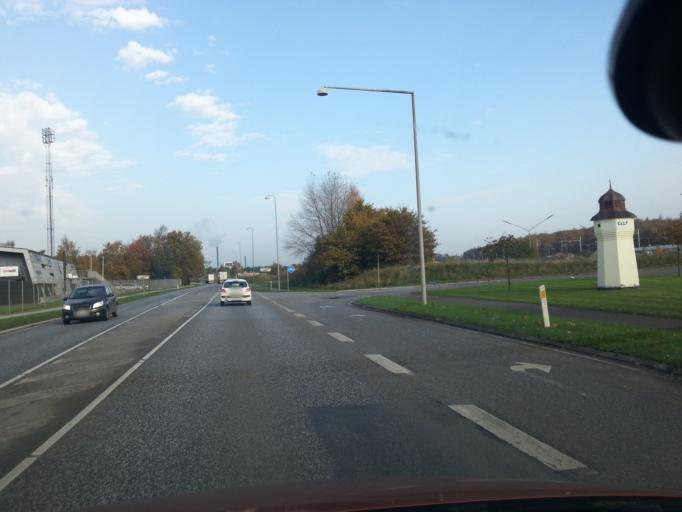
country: DK
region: Zealand
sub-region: Guldborgsund Kommune
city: Nykobing Falster
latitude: 54.7703
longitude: 11.8784
